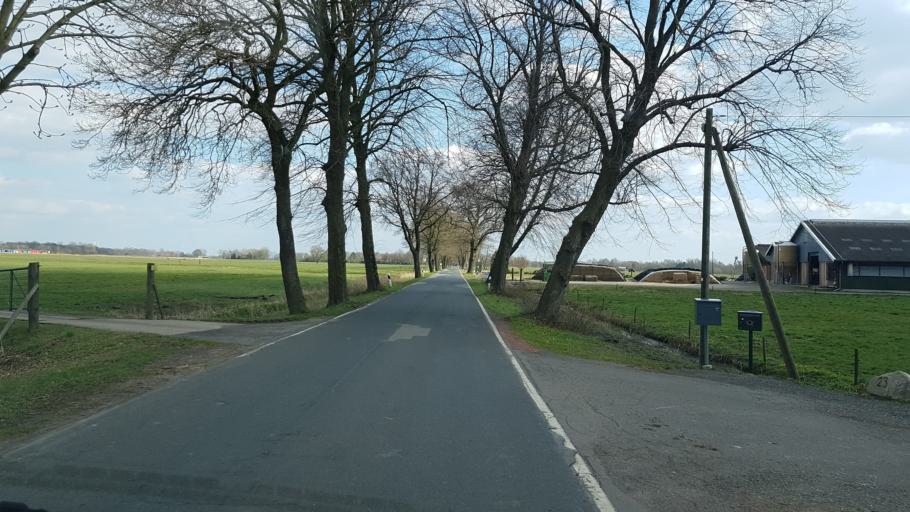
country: DE
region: Lower Saxony
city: Rastede
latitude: 53.2604
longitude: 8.2888
